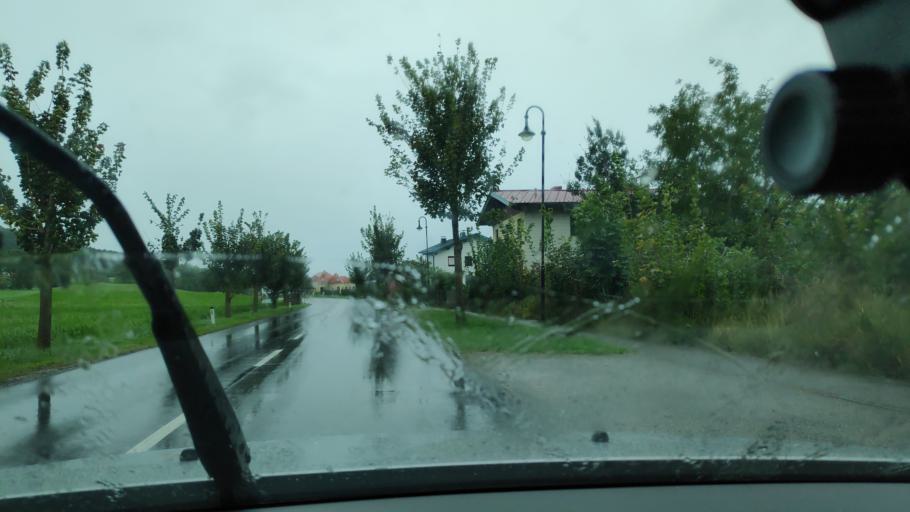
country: AT
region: Lower Austria
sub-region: Politischer Bezirk Neunkirchen
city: Grunbach am Schneeberg
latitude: 47.7966
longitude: 15.9943
